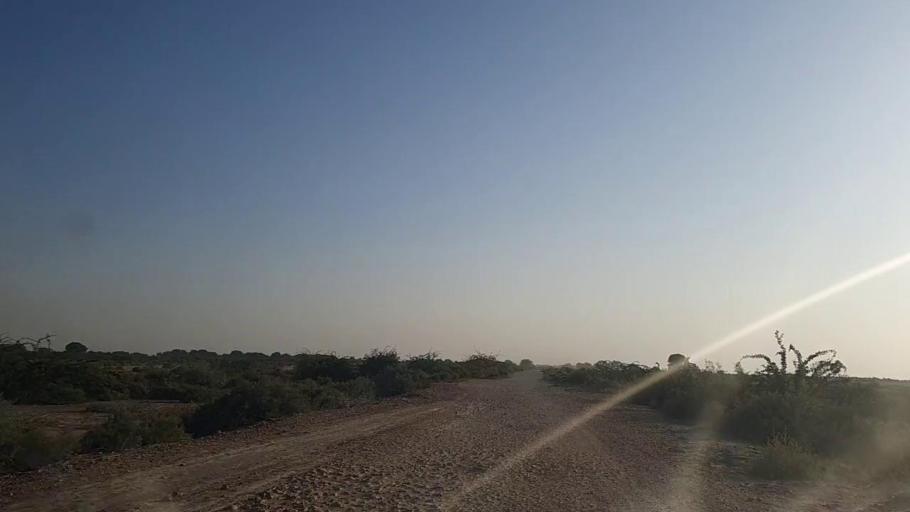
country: PK
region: Sindh
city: Jati
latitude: 24.4369
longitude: 68.1924
